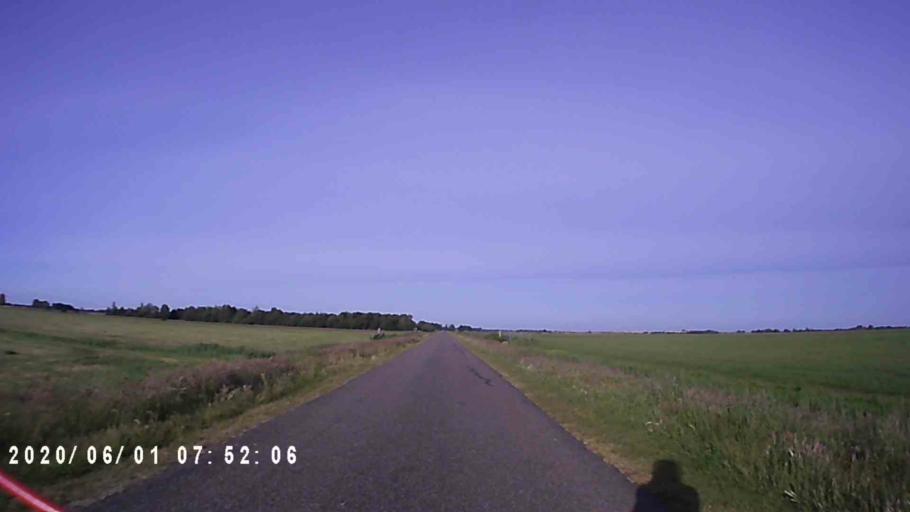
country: NL
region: Friesland
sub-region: Gemeente Dantumadiel
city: Rinsumageast
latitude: 53.2849
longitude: 5.9420
